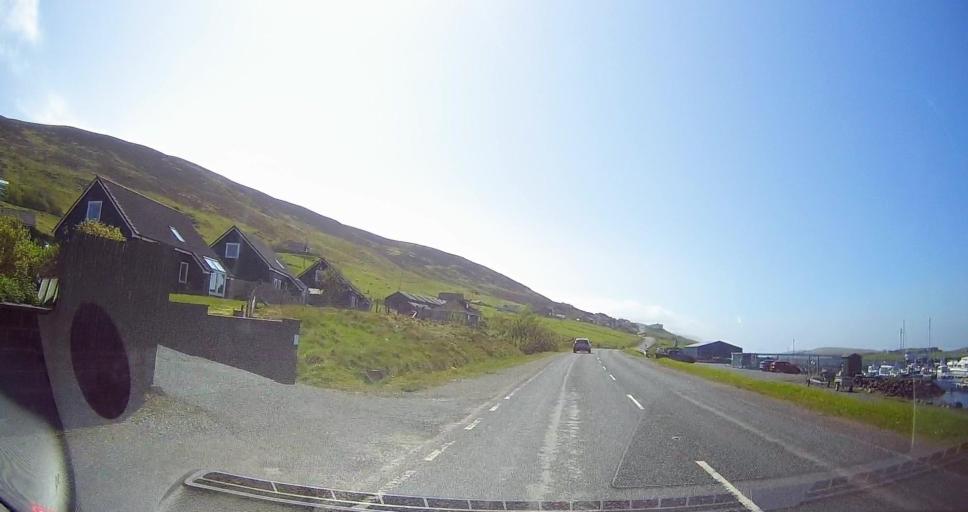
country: GB
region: Scotland
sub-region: Shetland Islands
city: Lerwick
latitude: 60.1377
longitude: -1.2666
